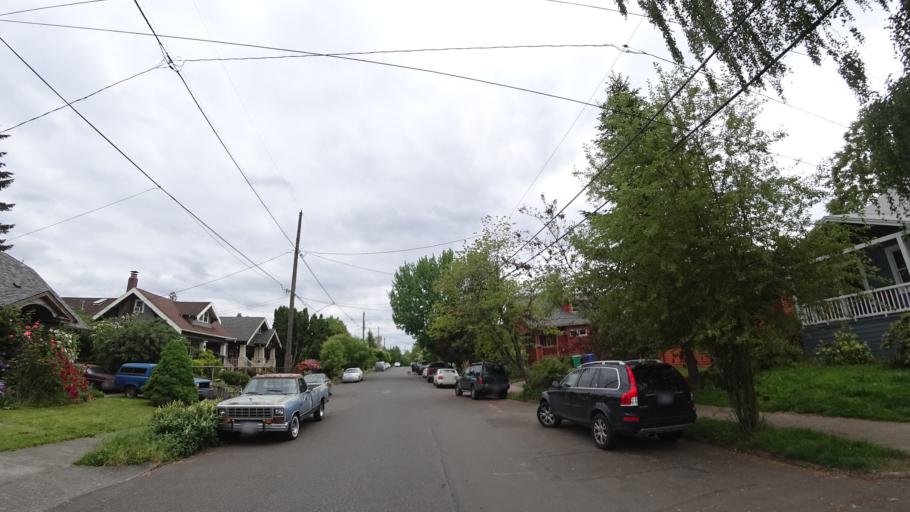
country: US
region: Oregon
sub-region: Multnomah County
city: Lents
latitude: 45.5101
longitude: -122.6142
